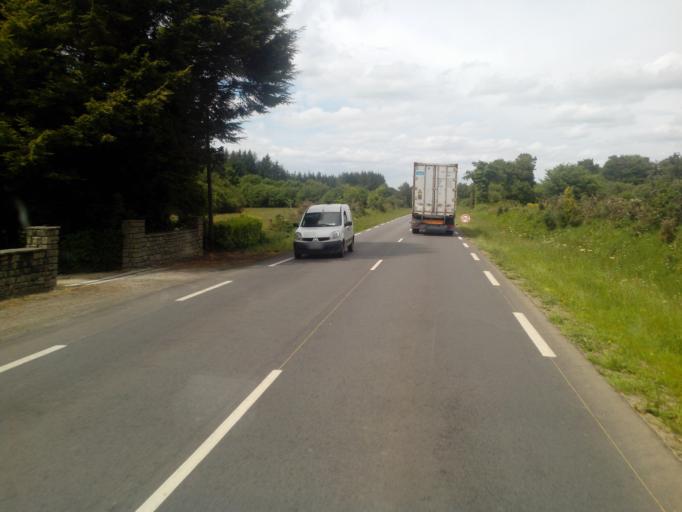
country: FR
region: Brittany
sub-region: Departement du Finistere
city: Guerlesquin
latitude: 48.5561
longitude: -3.5982
